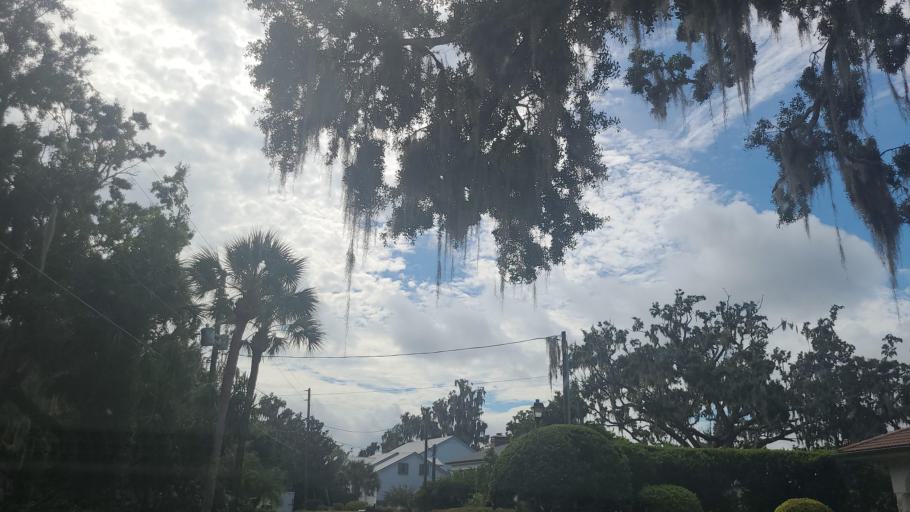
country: US
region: Florida
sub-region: Orange County
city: Lake Butler
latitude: 28.4973
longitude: -81.5455
